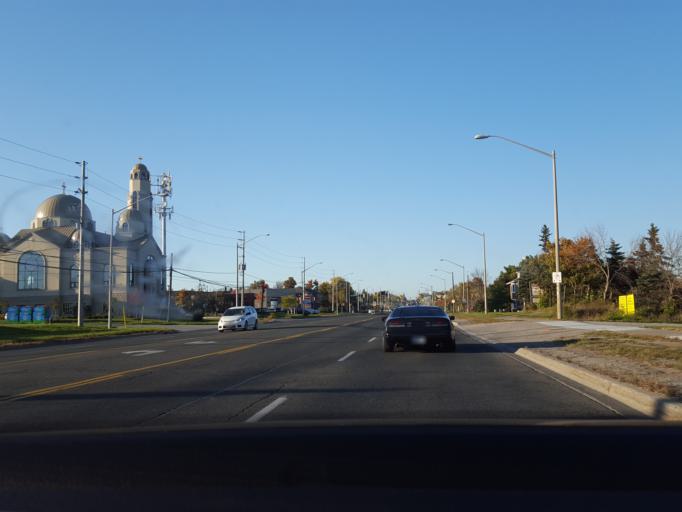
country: CA
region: Ontario
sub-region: York
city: Richmond Hill
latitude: 43.9028
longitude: -79.4445
